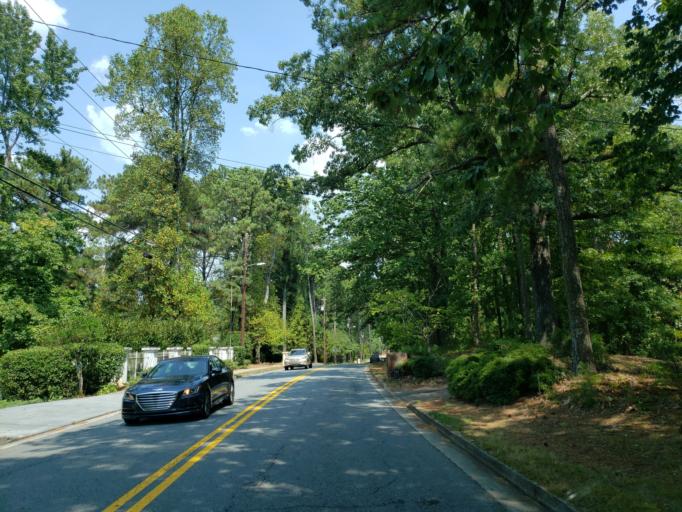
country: US
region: Georgia
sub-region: Fulton County
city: Sandy Springs
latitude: 33.9117
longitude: -84.4047
